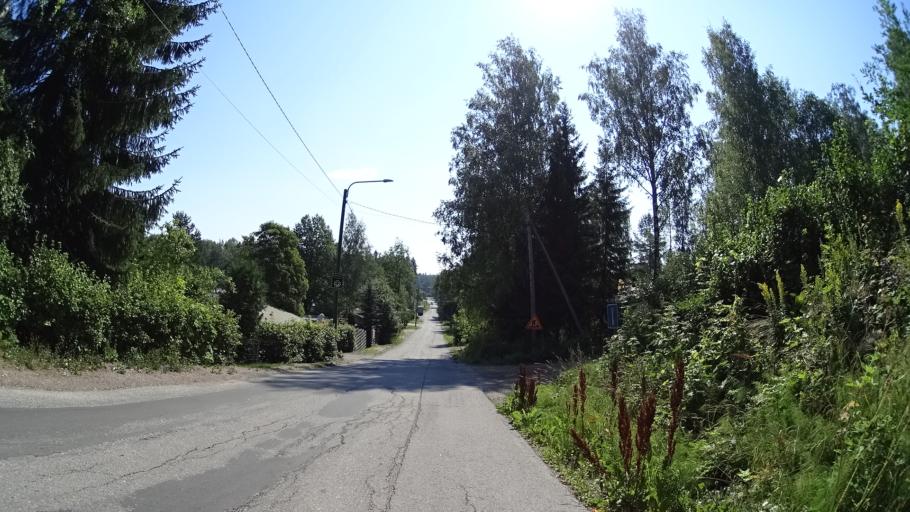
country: FI
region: Uusimaa
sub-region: Helsinki
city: Kerava
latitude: 60.3588
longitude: 25.0728
